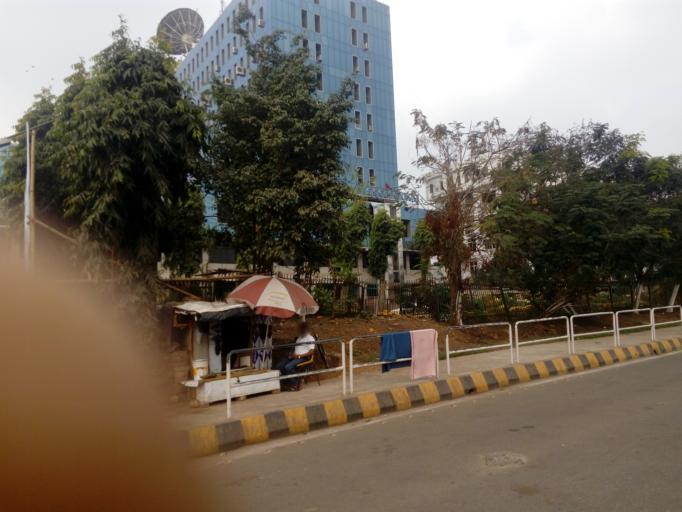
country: IN
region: Odisha
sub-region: Khordha
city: Bhubaneshwar
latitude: 20.2885
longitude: 85.8429
